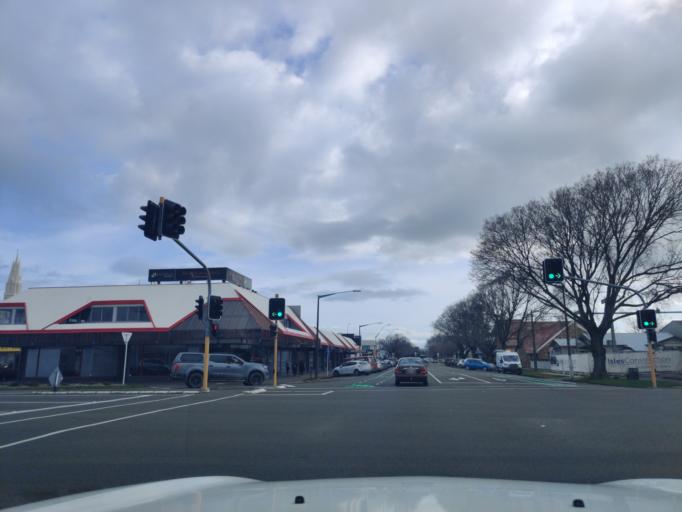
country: NZ
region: Manawatu-Wanganui
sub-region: Palmerston North City
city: Palmerston North
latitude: -40.3524
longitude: 175.6199
